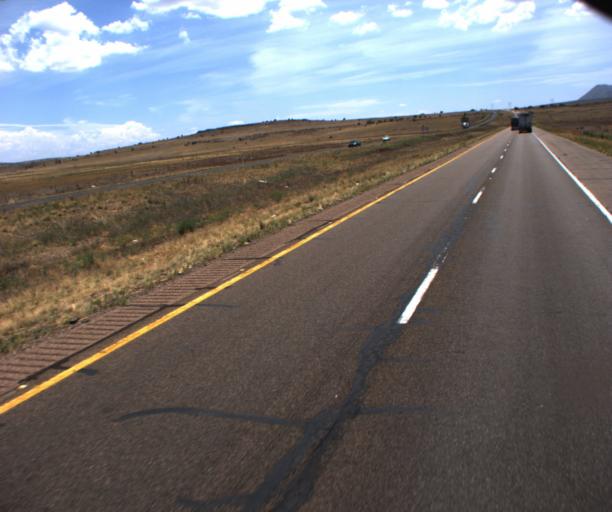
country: US
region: Arizona
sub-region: Yavapai County
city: Paulden
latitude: 35.2998
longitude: -112.8377
